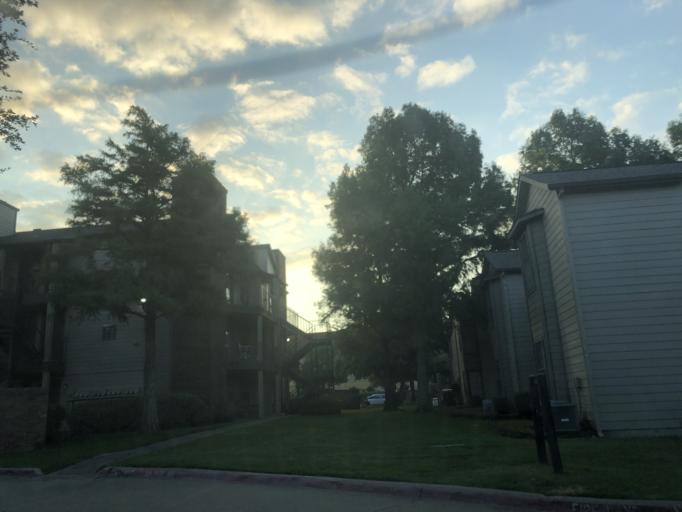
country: US
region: Texas
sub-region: Dallas County
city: Rowlett
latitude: 32.8500
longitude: -96.5751
